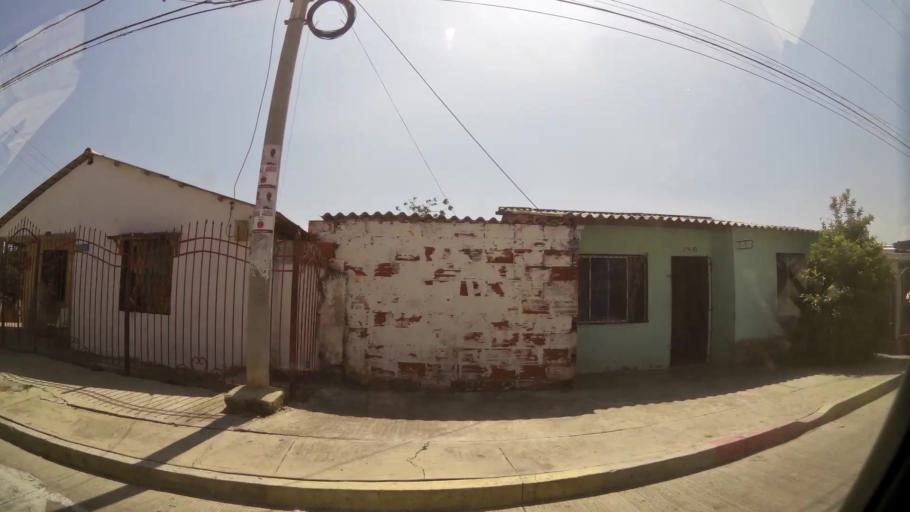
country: CO
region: Atlantico
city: Barranquilla
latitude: 10.9709
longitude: -74.8224
